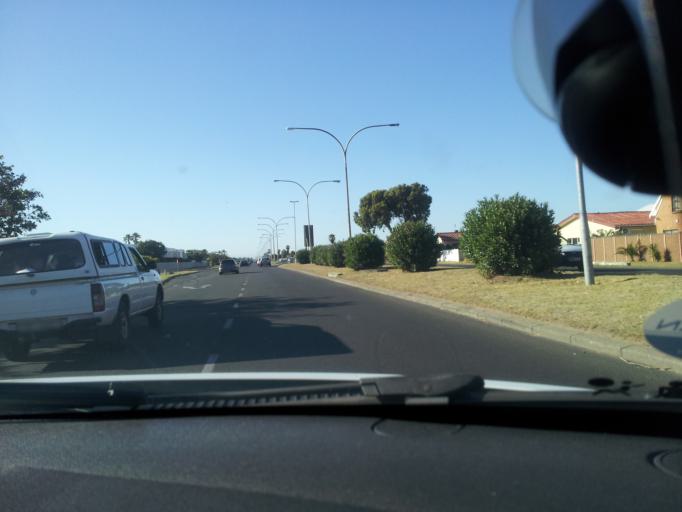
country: ZA
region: Western Cape
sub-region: Overberg District Municipality
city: Grabouw
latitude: -34.1461
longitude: 18.8553
